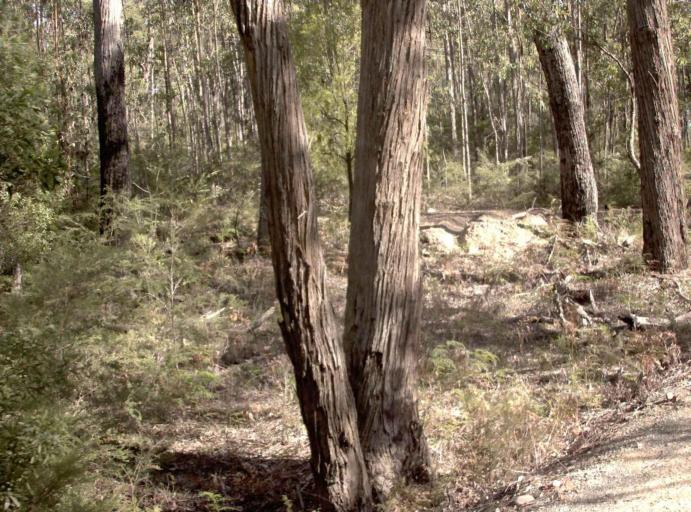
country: AU
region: Victoria
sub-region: East Gippsland
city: Lakes Entrance
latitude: -37.6742
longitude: 148.0560
